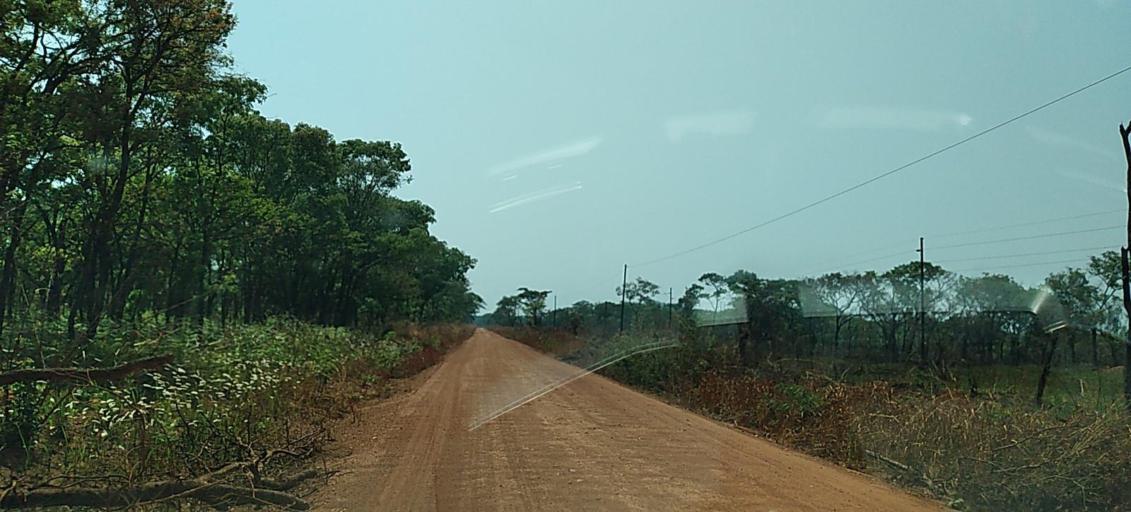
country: ZM
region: North-Western
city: Kansanshi
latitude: -11.9965
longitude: 26.6559
